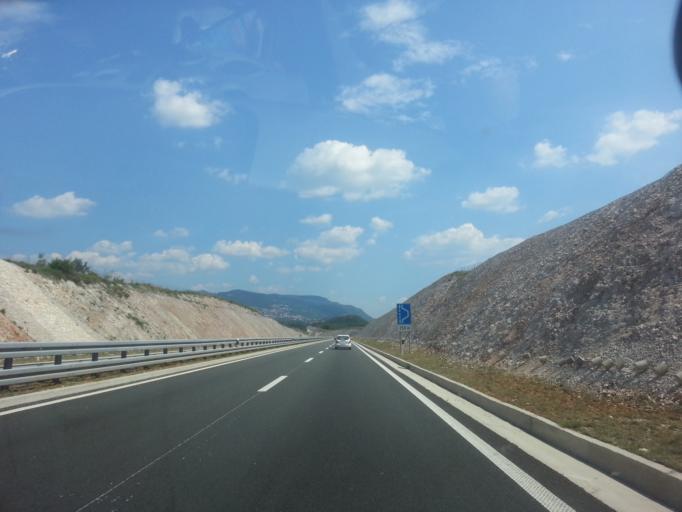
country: HR
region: Primorsko-Goranska
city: Krasica
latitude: 45.3064
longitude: 14.5520
